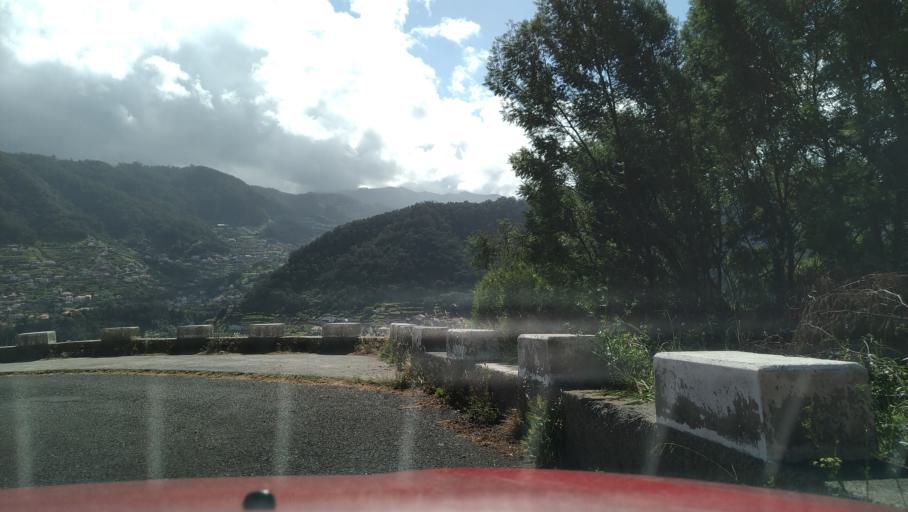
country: PT
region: Madeira
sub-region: Machico
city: Canical
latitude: 32.7389
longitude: -16.7728
